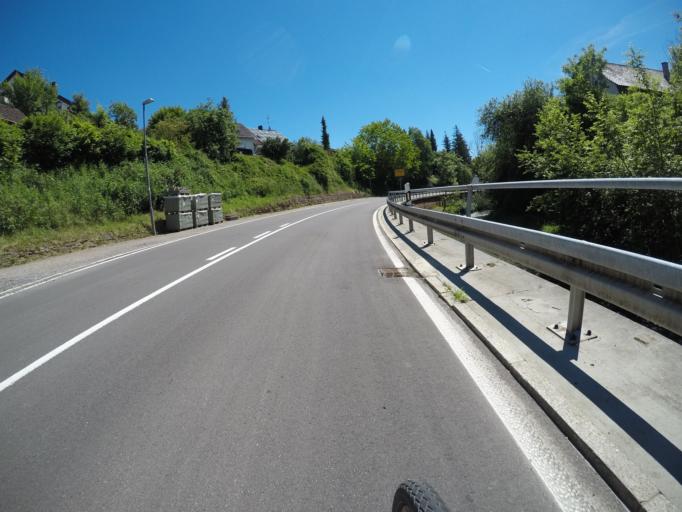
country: DE
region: Baden-Wuerttemberg
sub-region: Karlsruhe Region
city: Friolzheim
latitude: 48.8073
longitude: 8.8204
